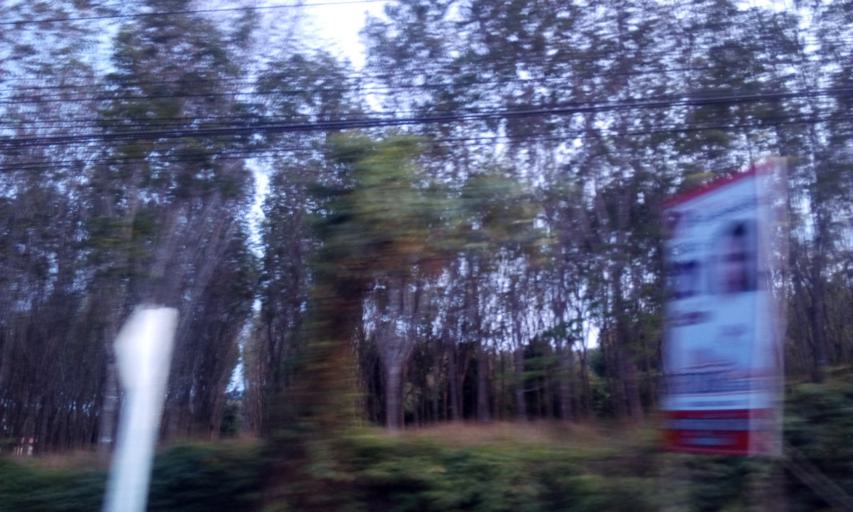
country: TH
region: Trat
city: Khao Saming
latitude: 12.2885
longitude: 102.3156
